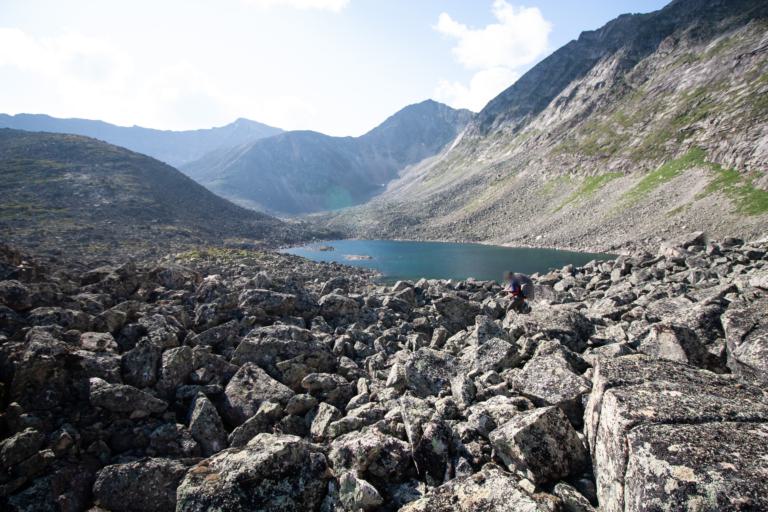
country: RU
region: Respublika Buryatiya
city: Novyy Uoyan
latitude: 56.3024
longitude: 111.2816
